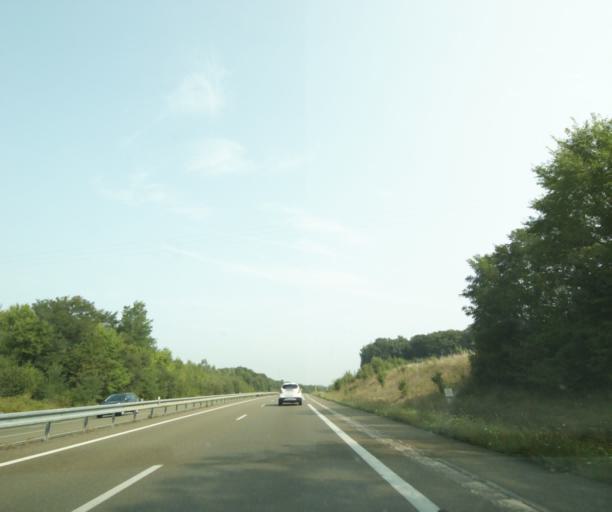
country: FR
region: Pays de la Loire
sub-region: Departement de la Sarthe
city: Neuville-sur-Sarthe
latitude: 48.0708
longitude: 0.1723
